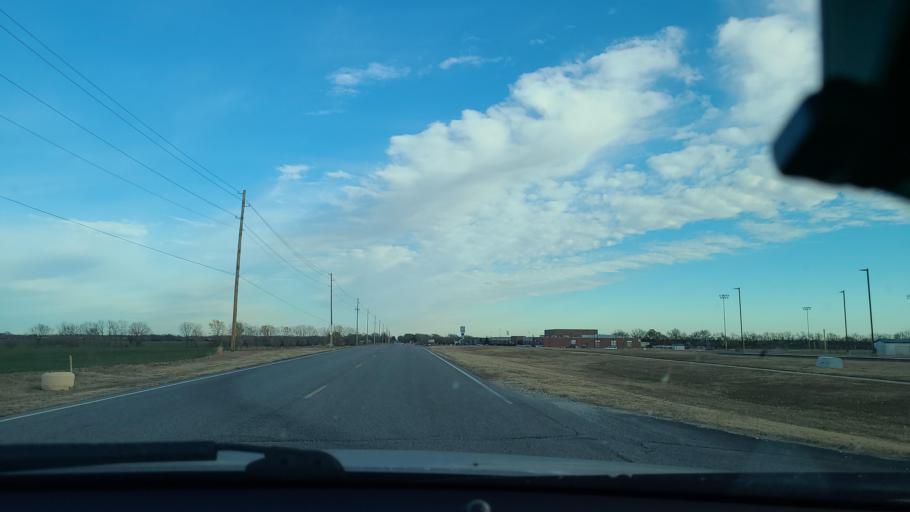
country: US
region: Kansas
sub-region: Sedgwick County
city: Goddard
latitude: 37.6496
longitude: -97.5679
